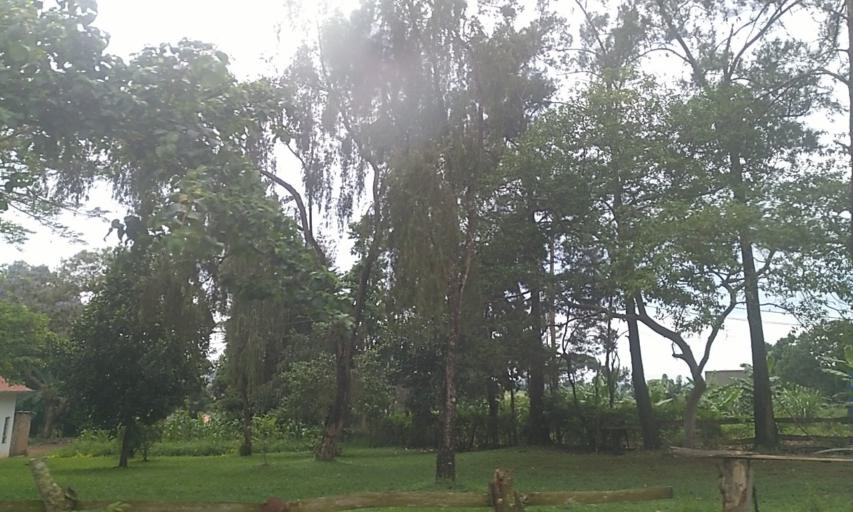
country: UG
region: Central Region
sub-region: Wakiso District
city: Bweyogerere
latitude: 0.3960
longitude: 32.6969
